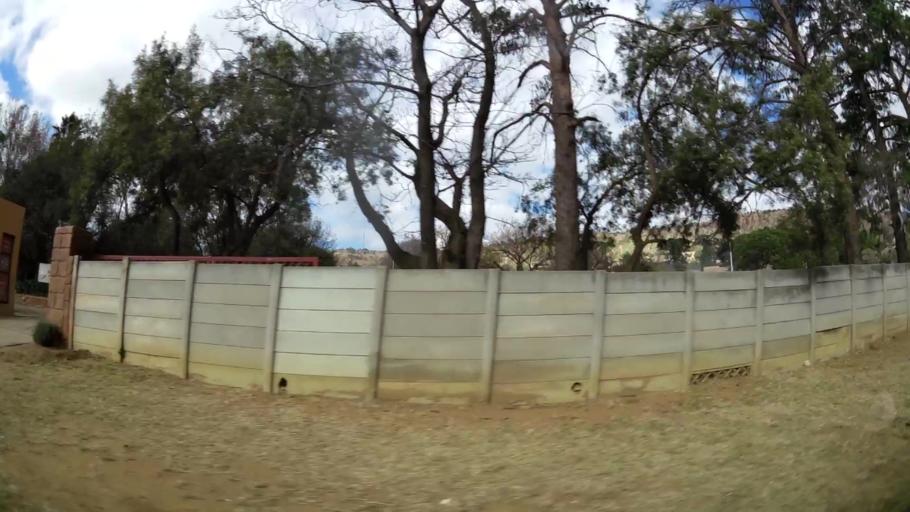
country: ZA
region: Gauteng
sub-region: West Rand District Municipality
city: Muldersdriseloop
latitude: -26.0930
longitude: 27.8563
